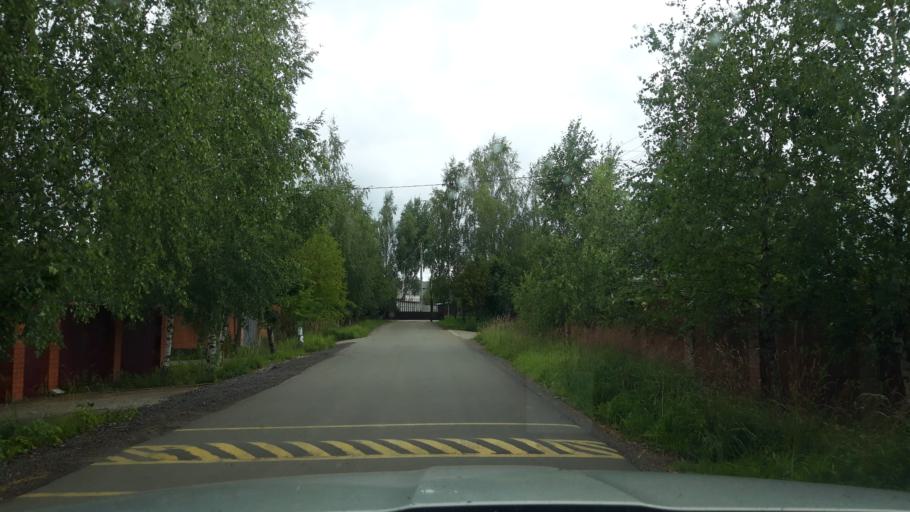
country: RU
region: Moskovskaya
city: Peshki
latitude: 56.1007
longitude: 37.0651
